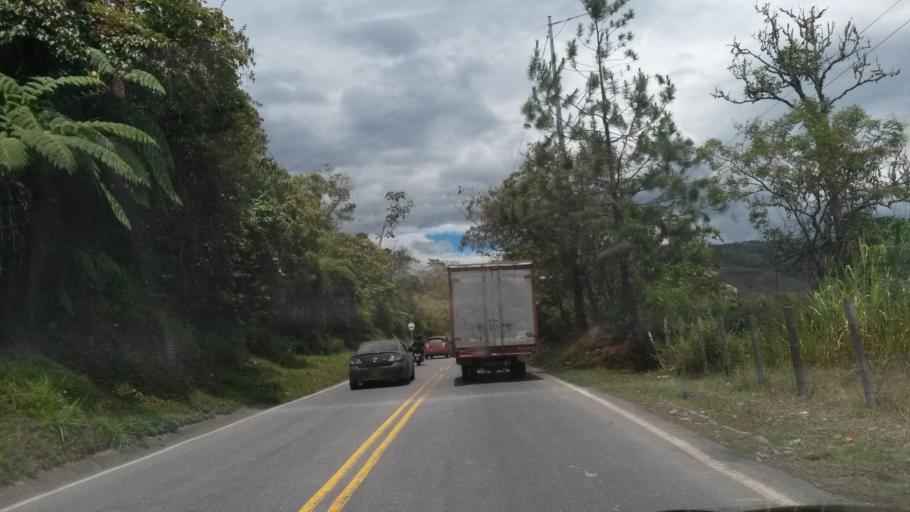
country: CO
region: Cauca
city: Rosas
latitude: 2.2599
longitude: -76.7538
